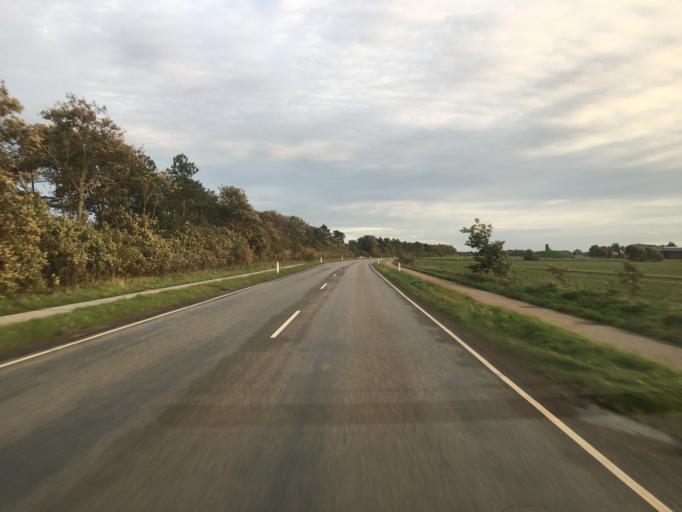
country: DK
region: South Denmark
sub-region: Tonder Kommune
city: Tonder
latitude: 54.9392
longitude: 8.8447
